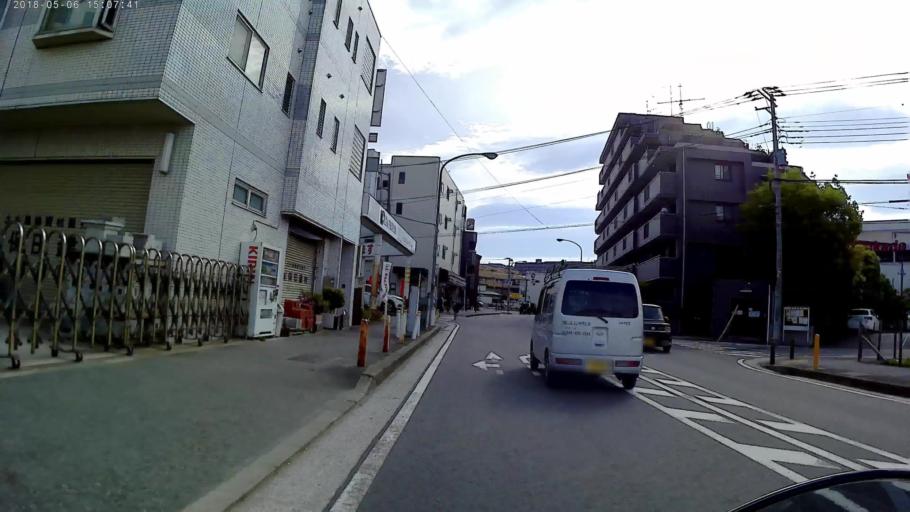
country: JP
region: Kanagawa
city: Yokohama
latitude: 35.4158
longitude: 139.5965
